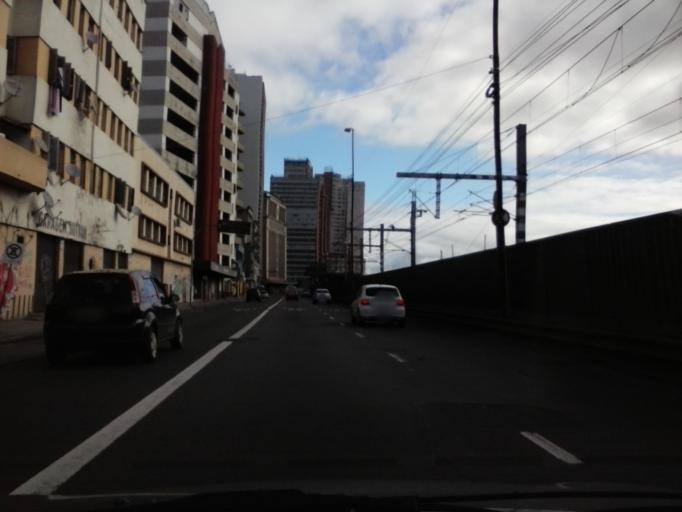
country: BR
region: Rio Grande do Sul
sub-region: Porto Alegre
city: Porto Alegre
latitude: -30.0253
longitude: -51.2252
